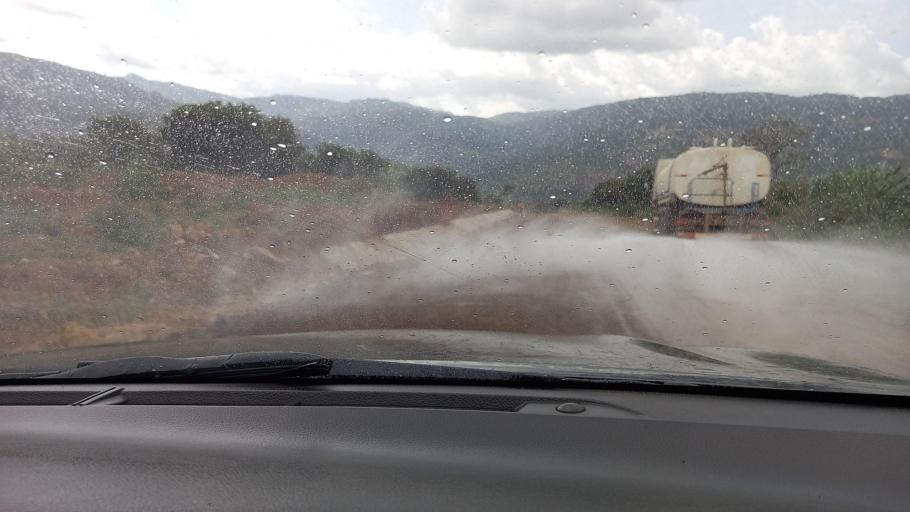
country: ET
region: Southern Nations, Nationalities, and People's Region
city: Mizan Teferi
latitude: 6.1867
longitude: 35.6903
